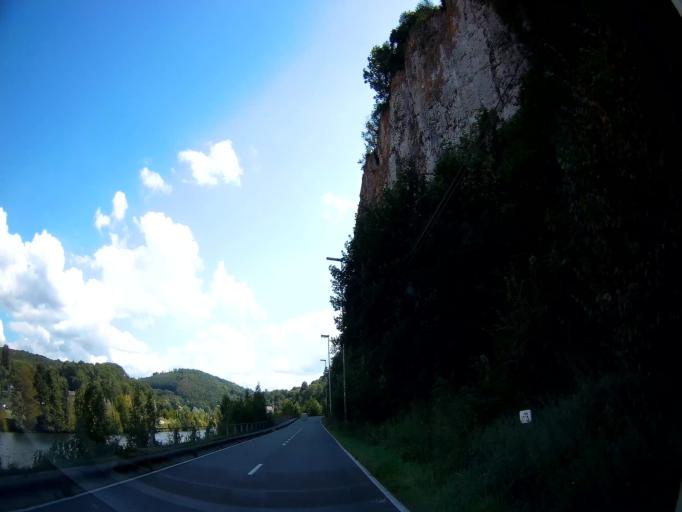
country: BE
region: Wallonia
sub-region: Province de Namur
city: Yvoir
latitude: 50.3414
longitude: 4.8586
